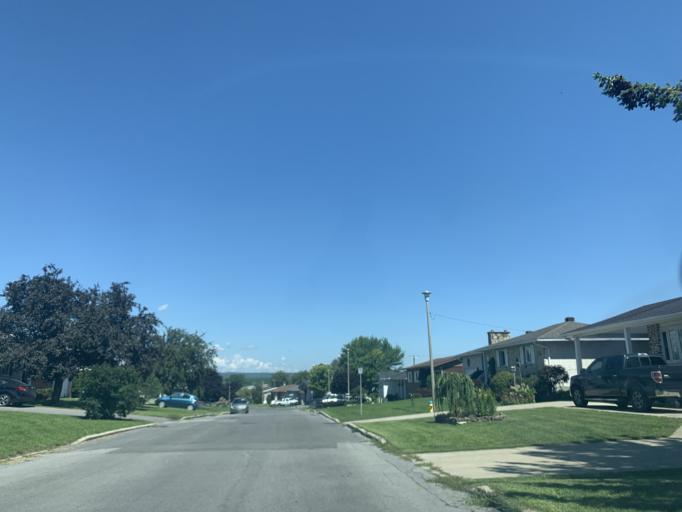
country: CA
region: Ontario
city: Hawkesbury
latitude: 45.6050
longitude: -74.5998
